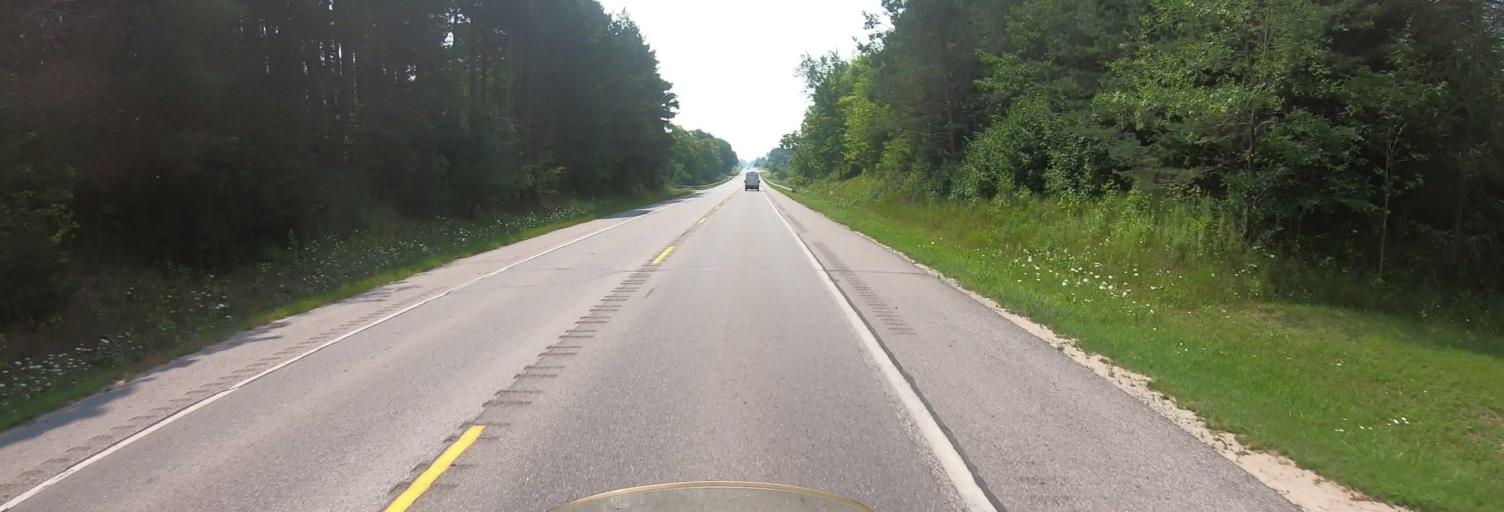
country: US
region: Michigan
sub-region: Luce County
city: Newberry
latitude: 46.3229
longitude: -85.5097
